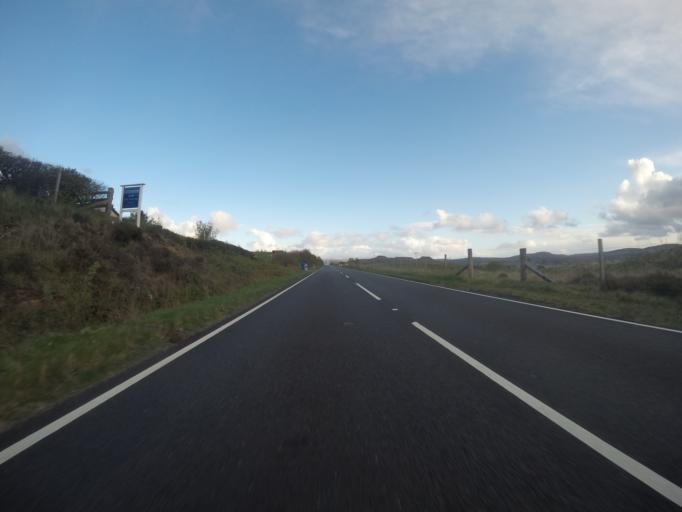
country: GB
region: Scotland
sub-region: Highland
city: Portree
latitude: 57.4972
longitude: -6.3226
